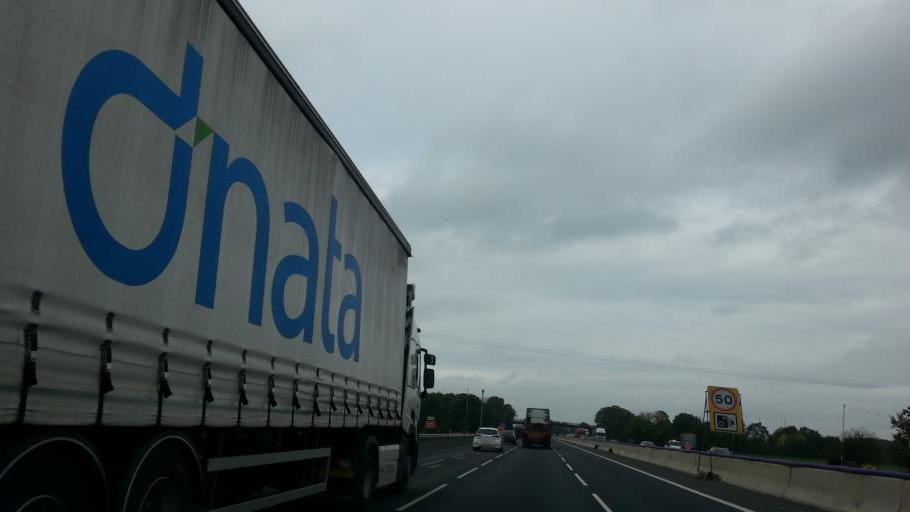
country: GB
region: England
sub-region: Cheshire East
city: Sandbach
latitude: 53.1658
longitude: -2.3557
